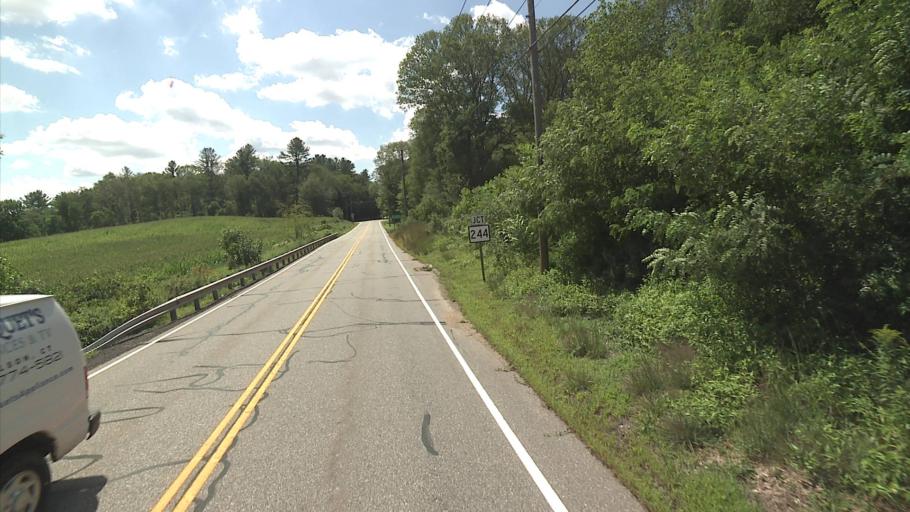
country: US
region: Connecticut
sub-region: Windham County
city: South Woodstock
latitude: 41.8895
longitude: -72.0806
